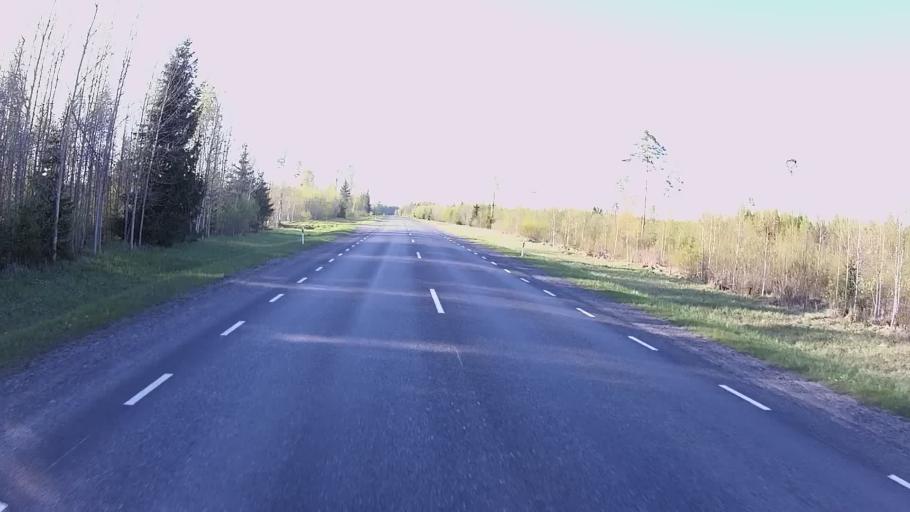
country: EE
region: Viljandimaa
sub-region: Vohma linn
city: Vohma
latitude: 58.6134
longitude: 25.5710
